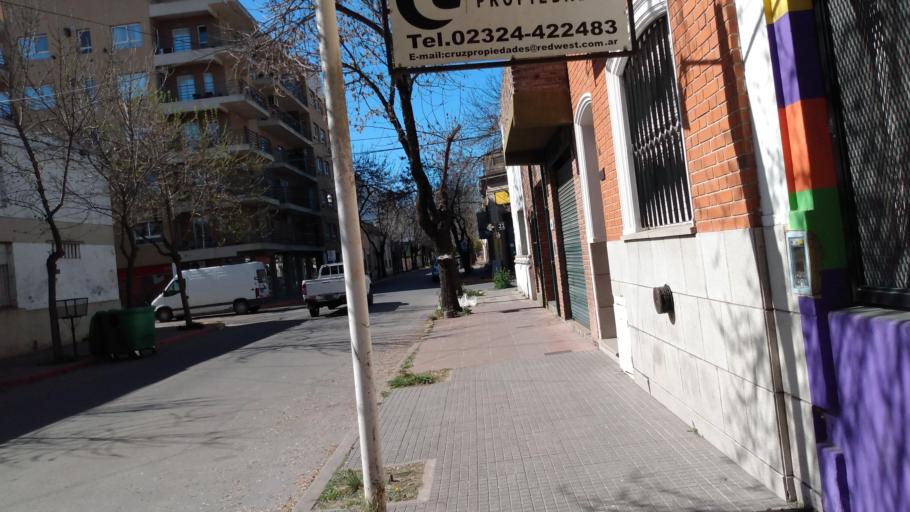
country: AR
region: Buenos Aires
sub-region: Partido de Mercedes
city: Mercedes
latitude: -34.6523
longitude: -59.4291
